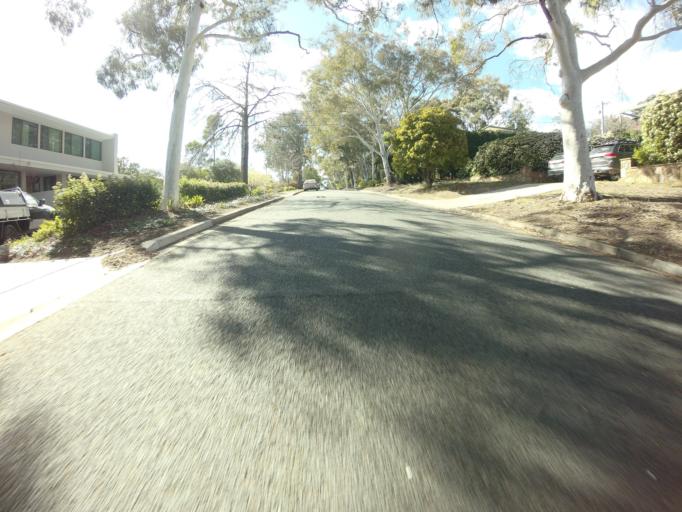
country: AU
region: Australian Capital Territory
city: Canberra
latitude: -35.2932
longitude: 149.1521
